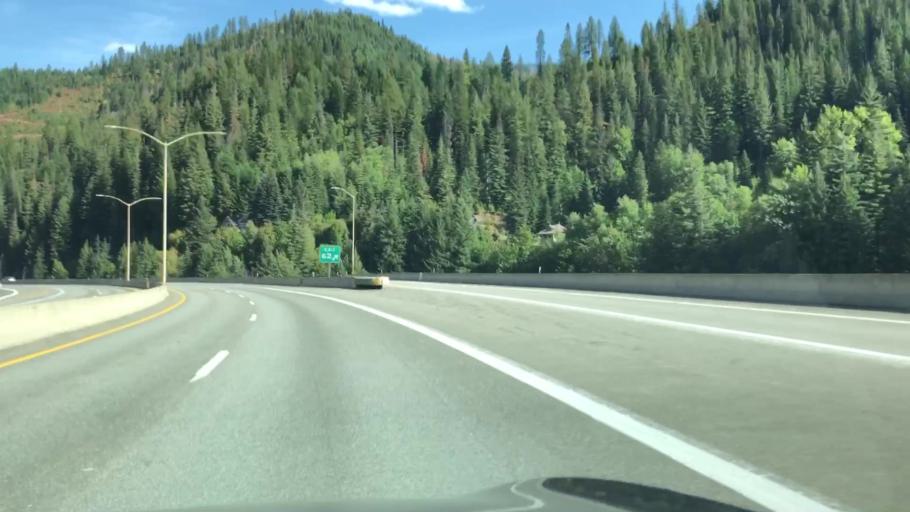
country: US
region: Idaho
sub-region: Shoshone County
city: Wallace
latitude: 47.4721
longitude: -115.9207
